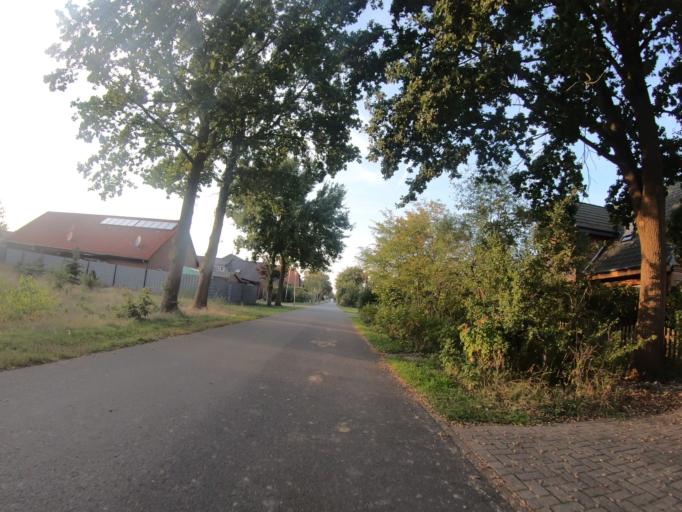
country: DE
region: Lower Saxony
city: Wagenhoff
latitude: 52.5509
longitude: 10.5281
